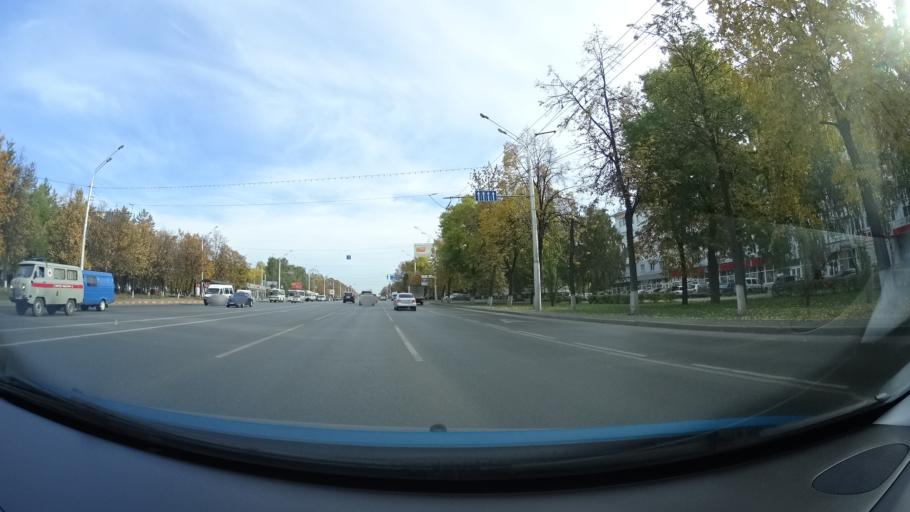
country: RU
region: Bashkortostan
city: Ufa
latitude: 54.7654
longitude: 56.0174
